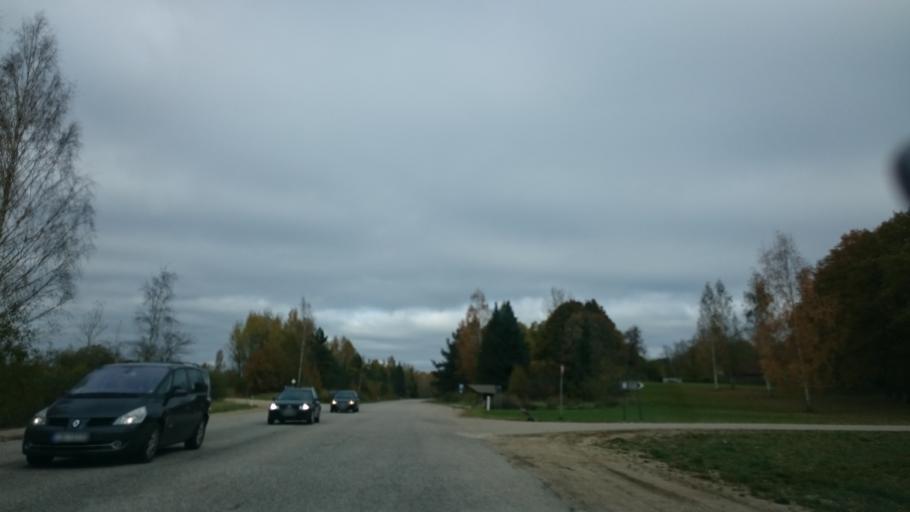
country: LV
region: Amatas Novads
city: Drabesi
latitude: 57.2346
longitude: 25.2535
